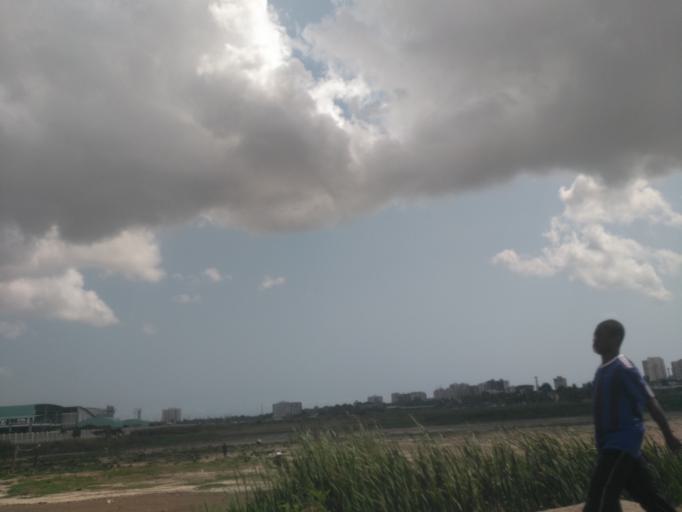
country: TZ
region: Dar es Salaam
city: Dar es Salaam
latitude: -6.8155
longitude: 39.2665
